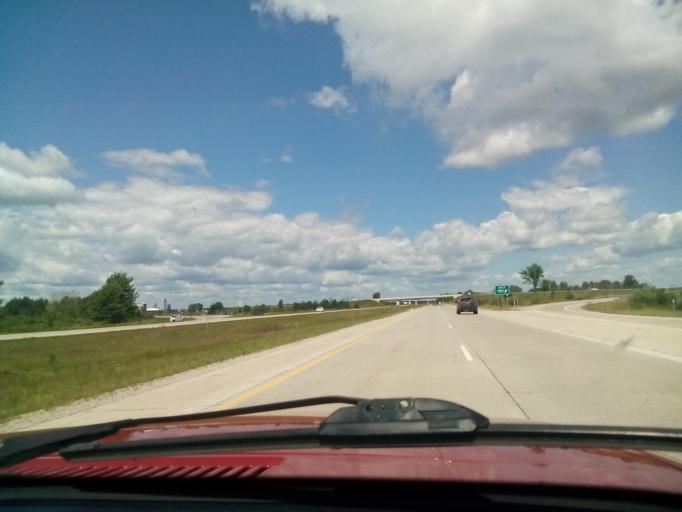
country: US
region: Michigan
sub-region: Bay County
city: Pinconning
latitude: 43.8491
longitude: -84.0204
